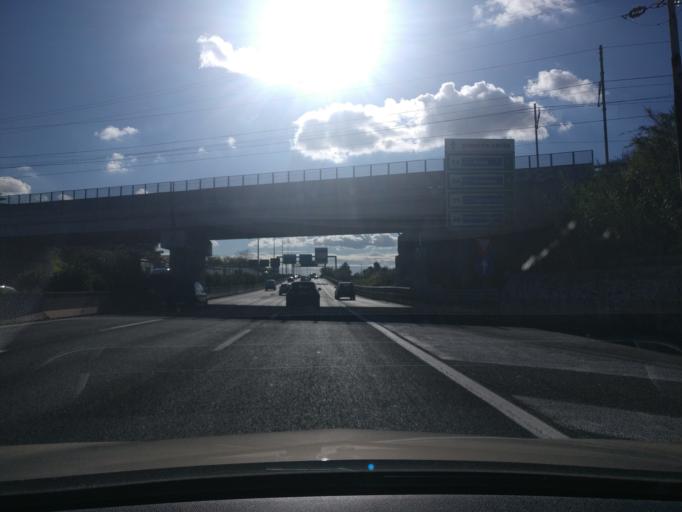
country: IT
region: Latium
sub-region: Citta metropolitana di Roma Capitale
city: Ciampino
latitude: 41.8208
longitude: 12.5791
